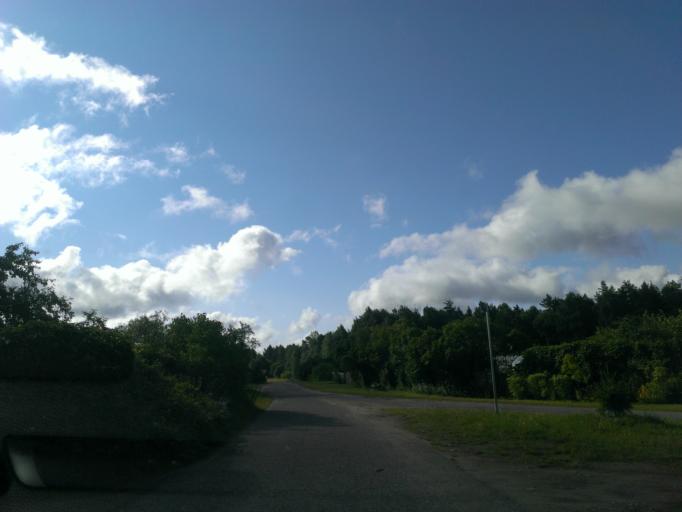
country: LV
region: Incukalns
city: Vangazi
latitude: 57.1023
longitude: 24.5263
